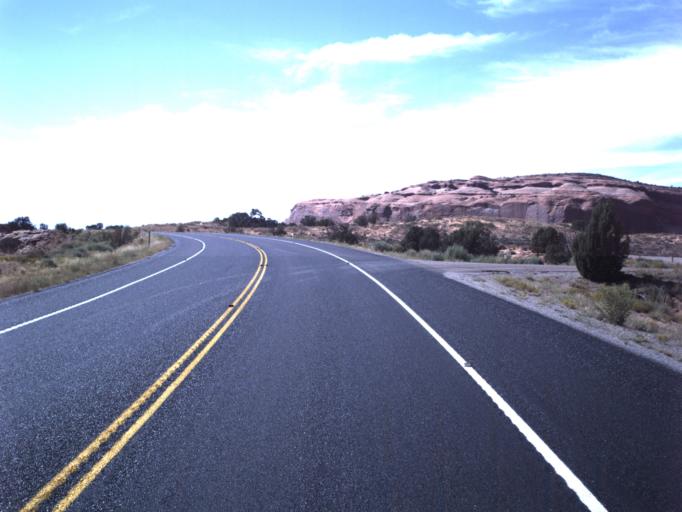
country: US
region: Utah
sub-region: Grand County
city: Moab
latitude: 38.6367
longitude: -109.7846
